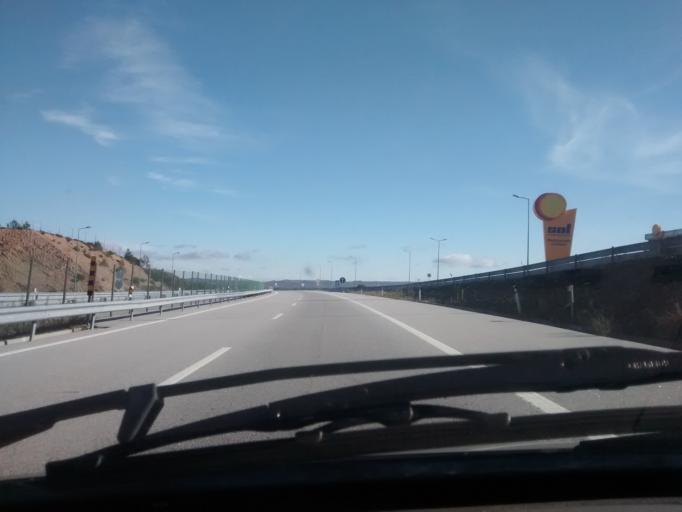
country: PT
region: Vila Real
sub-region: Vila Pouca de Aguiar
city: Vila Pouca de Aguiar
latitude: 41.5033
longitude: -7.7202
